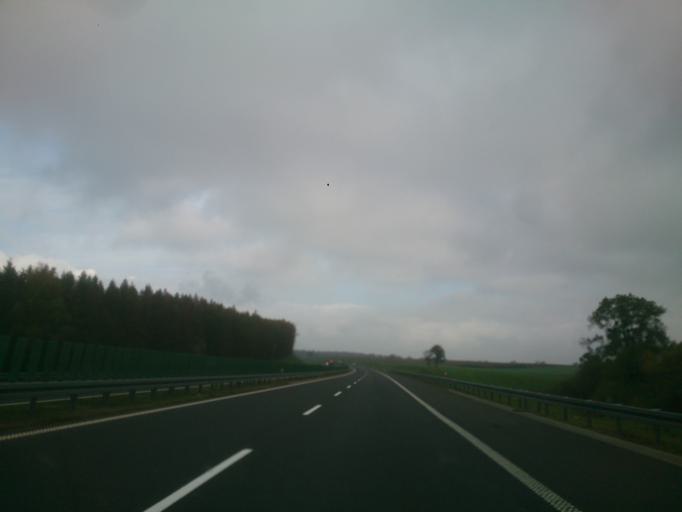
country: PL
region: Pomeranian Voivodeship
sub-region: Powiat starogardzki
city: Smetowo Graniczne
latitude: 53.8153
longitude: 18.6281
